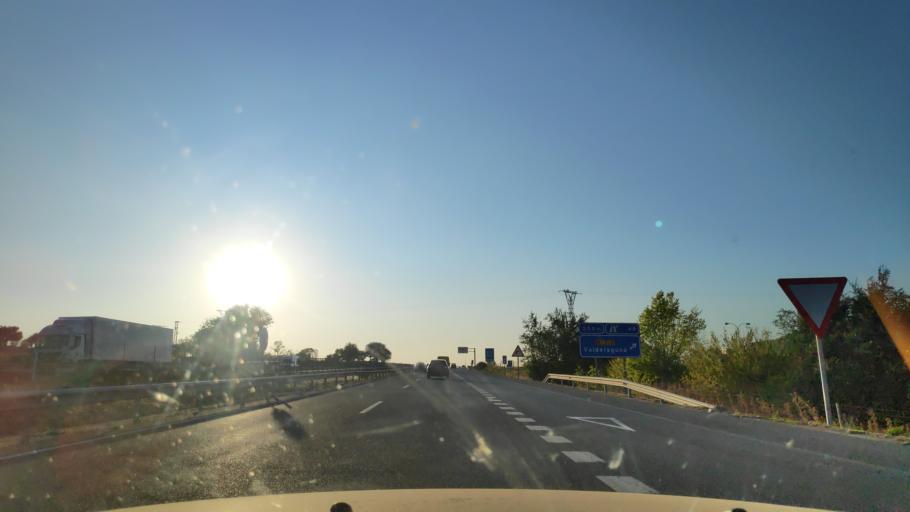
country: ES
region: Madrid
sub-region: Provincia de Madrid
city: Villarejo de Salvanes
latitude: 40.1679
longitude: -3.2863
